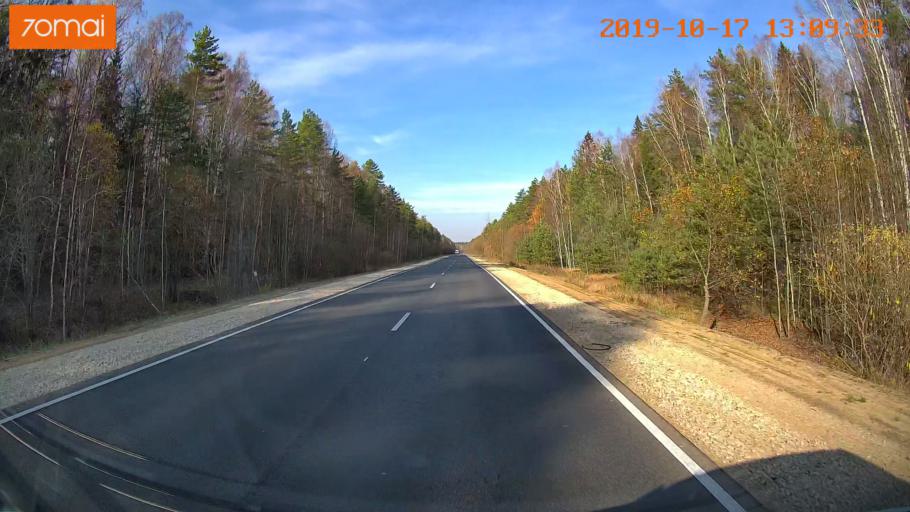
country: RU
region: Rjazan
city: Syntul
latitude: 55.0056
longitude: 41.2623
